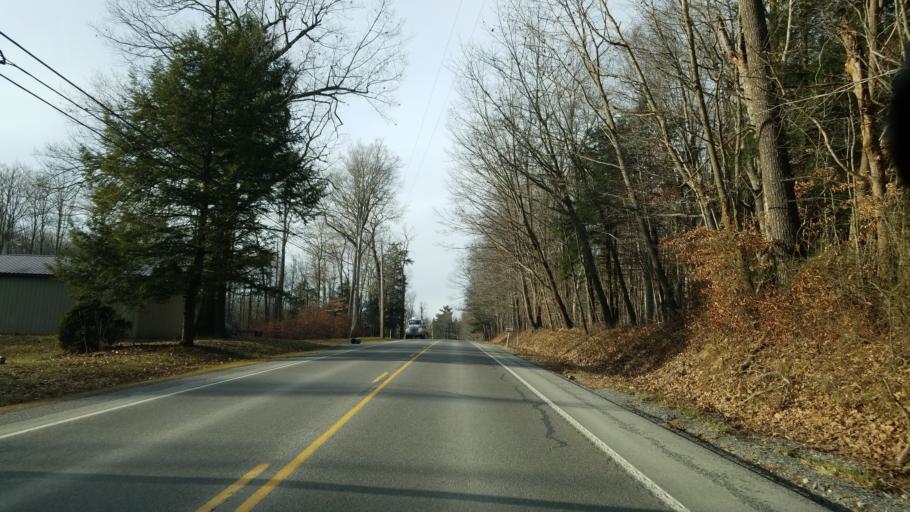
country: US
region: Pennsylvania
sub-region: Clearfield County
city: DuBois
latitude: 41.0280
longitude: -78.6735
